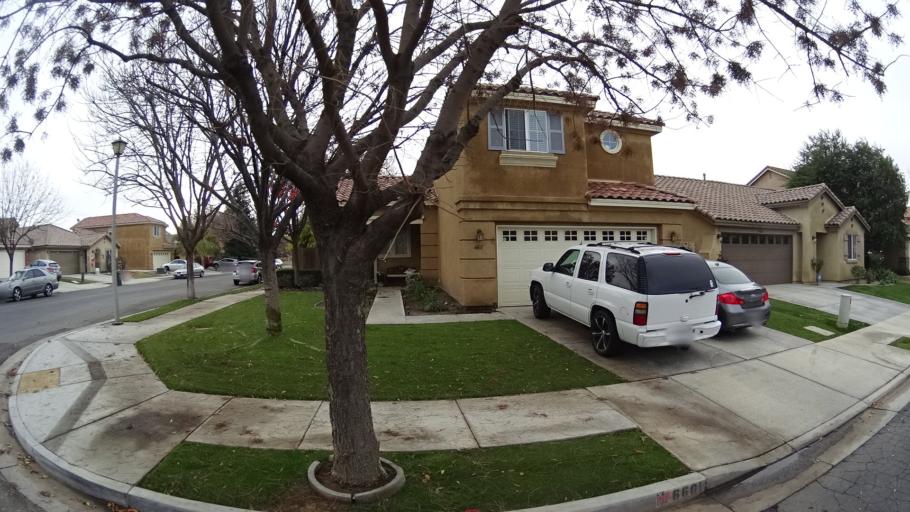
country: US
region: California
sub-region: Kern County
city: Greenfield
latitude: 35.2986
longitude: -119.0753
